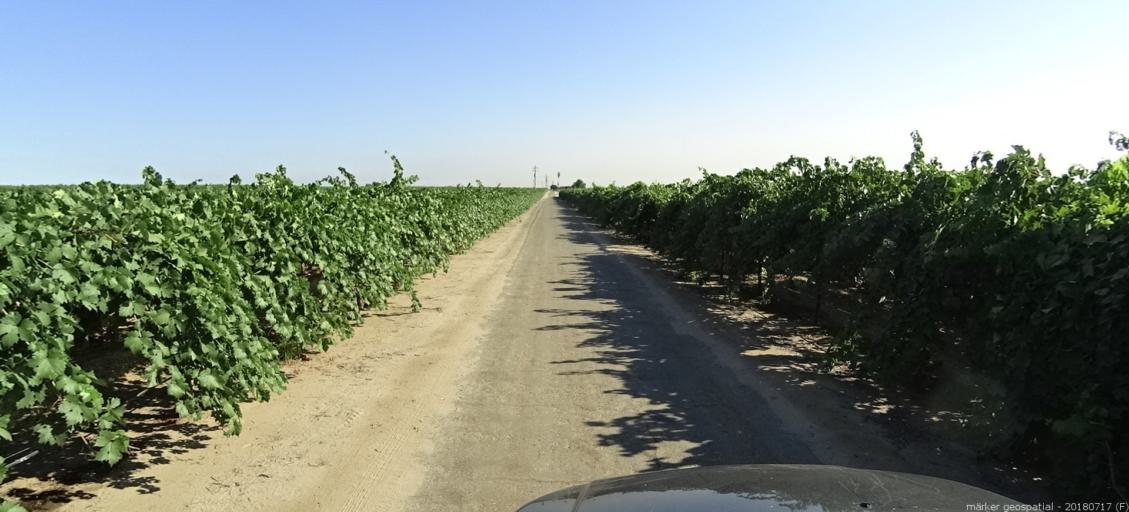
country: US
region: California
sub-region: Madera County
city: Madera Acres
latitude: 37.0401
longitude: -120.1266
